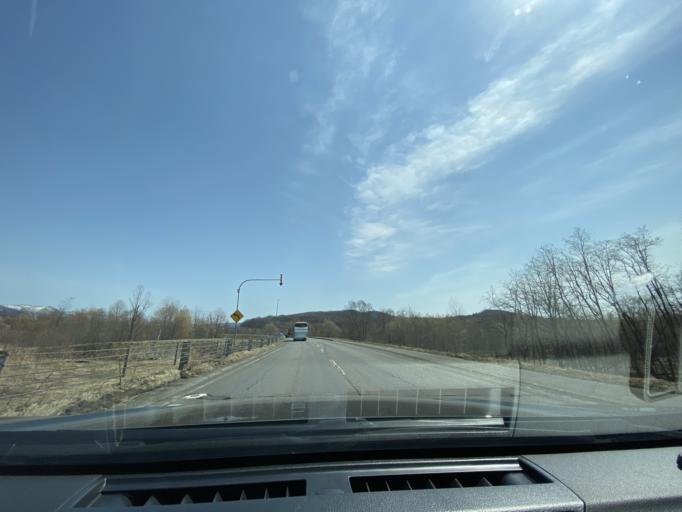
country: JP
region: Hokkaido
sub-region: Asahikawa-shi
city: Asahikawa
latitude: 43.8984
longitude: 142.5481
